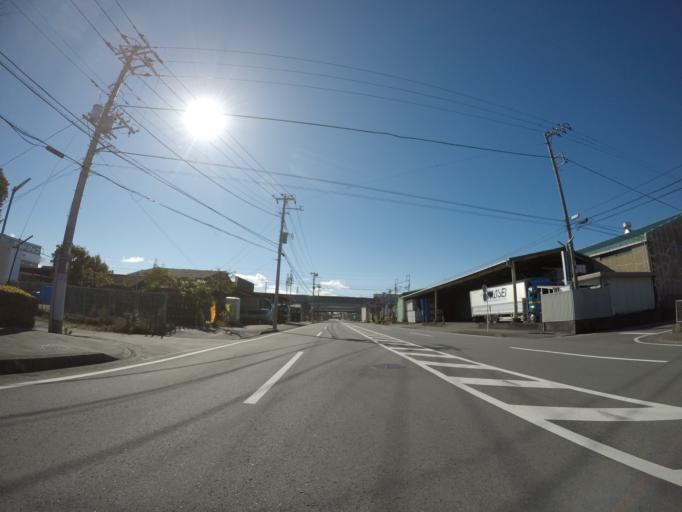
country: JP
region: Shizuoka
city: Fuji
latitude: 35.1518
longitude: 138.7043
